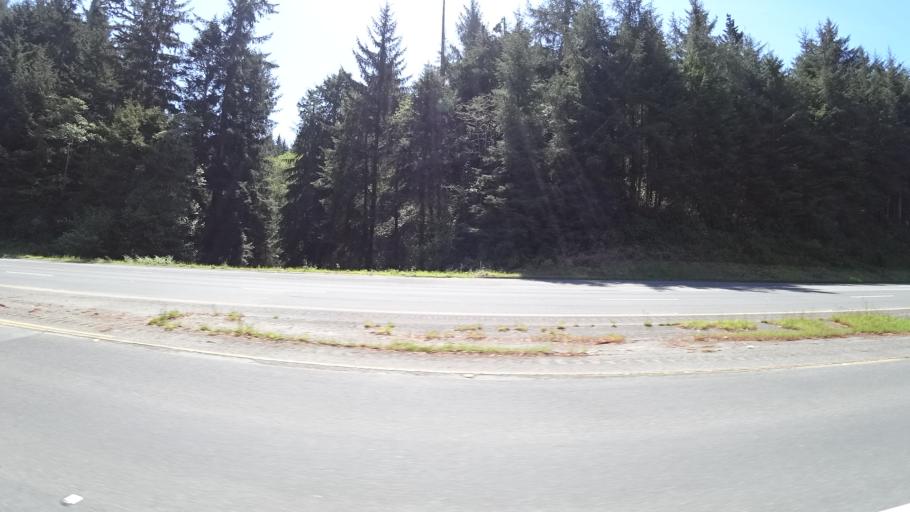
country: US
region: California
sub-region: Humboldt County
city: Westhaven-Moonstone
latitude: 41.1372
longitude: -124.1442
